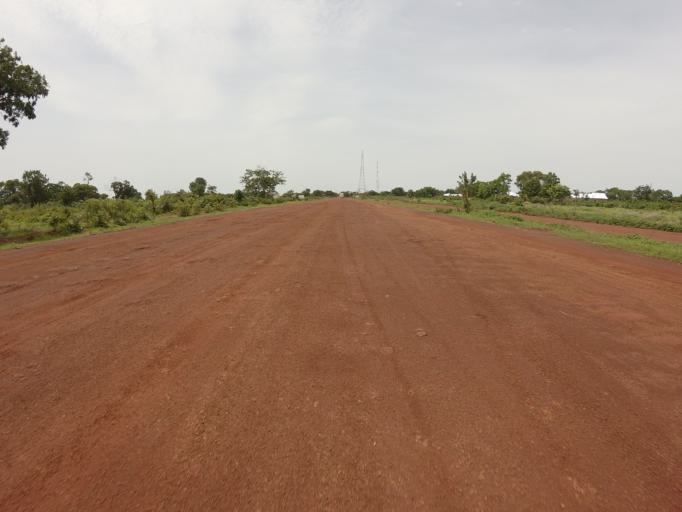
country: GH
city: Kpandae
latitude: 8.8764
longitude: 0.0394
